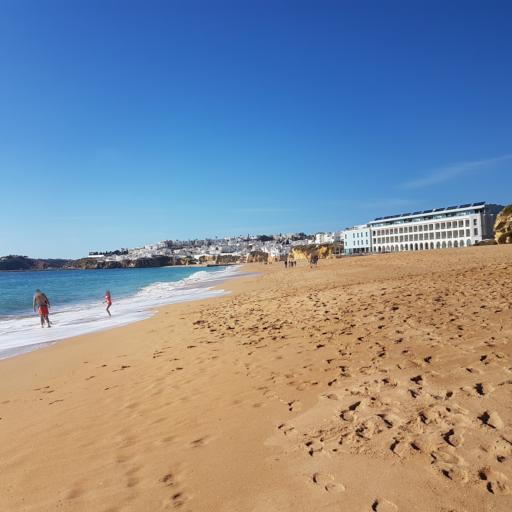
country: PT
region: Faro
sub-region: Albufeira
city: Albufeira
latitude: 37.0848
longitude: -8.2411
